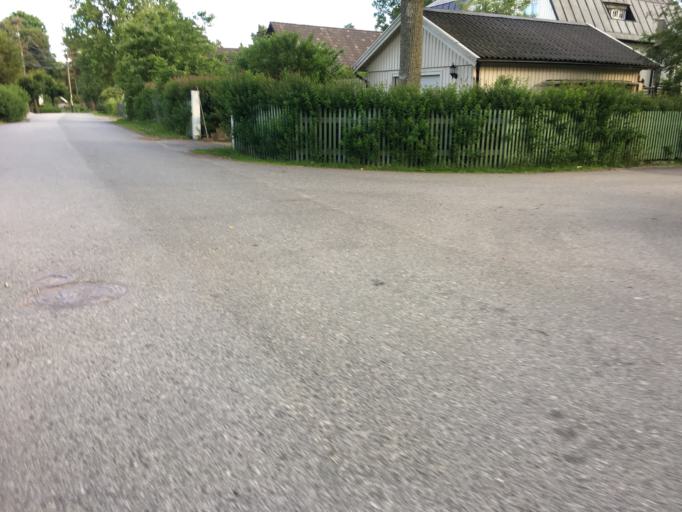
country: SE
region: Stockholm
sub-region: Nacka Kommun
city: Fisksatra
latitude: 59.3188
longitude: 18.2370
